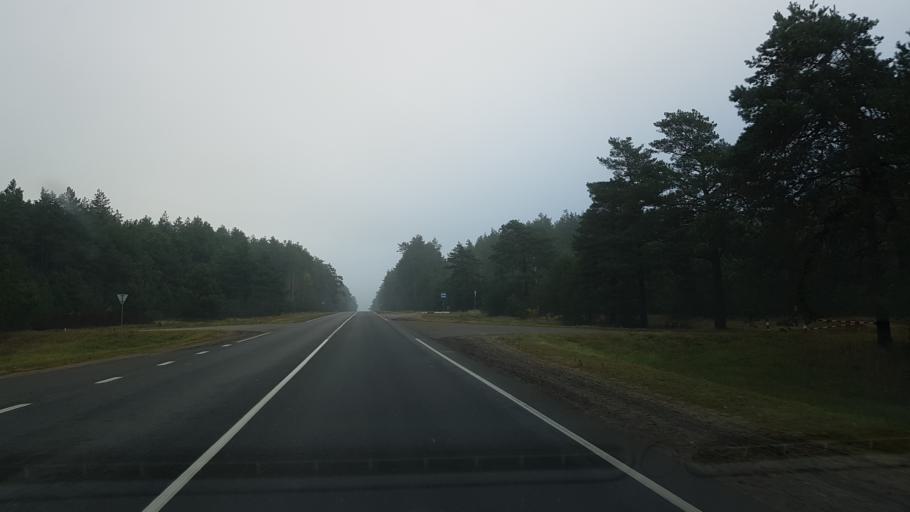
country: BY
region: Mogilev
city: Babruysk
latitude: 53.1611
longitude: 29.3232
